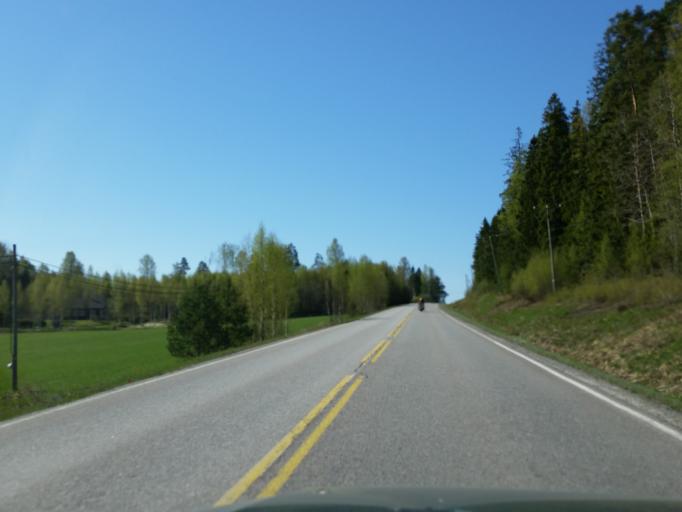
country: FI
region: Uusimaa
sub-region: Helsinki
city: Siuntio
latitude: 60.1919
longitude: 24.2486
